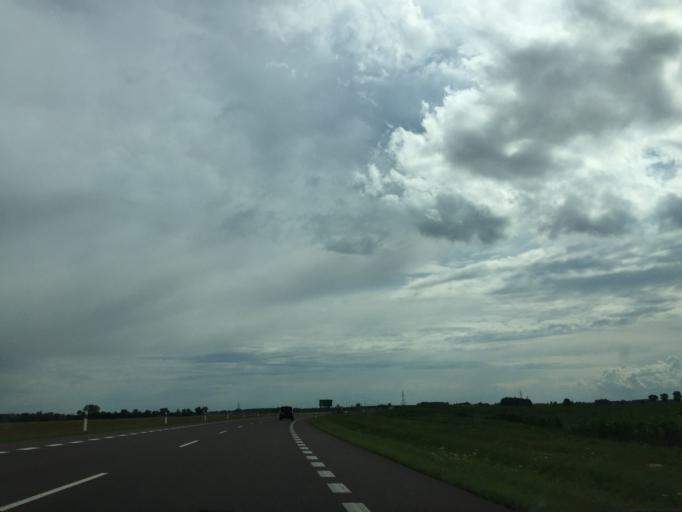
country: PL
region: Lublin Voivodeship
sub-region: Powiat bialski
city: Miedzyrzec Podlaski
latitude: 52.0123
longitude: 22.7593
